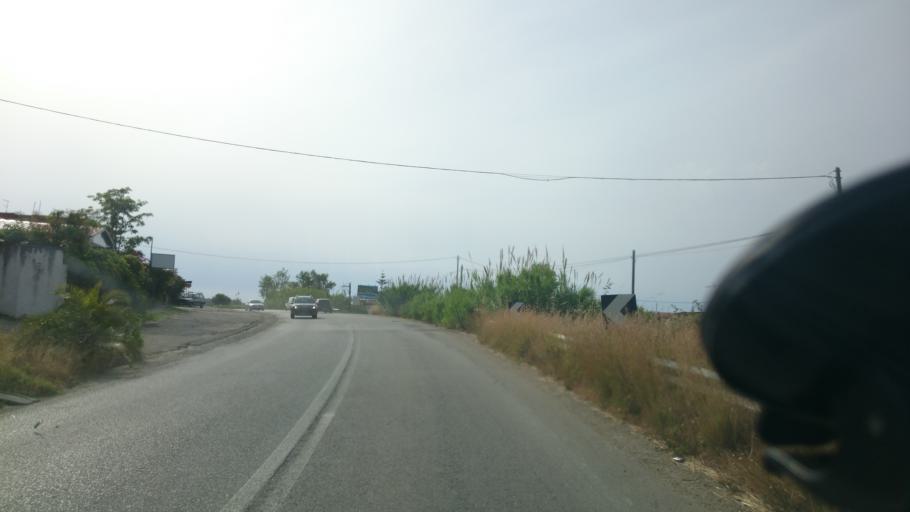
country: IT
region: Calabria
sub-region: Provincia di Vibo-Valentia
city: Pannaconi
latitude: 38.7150
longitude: 16.0617
